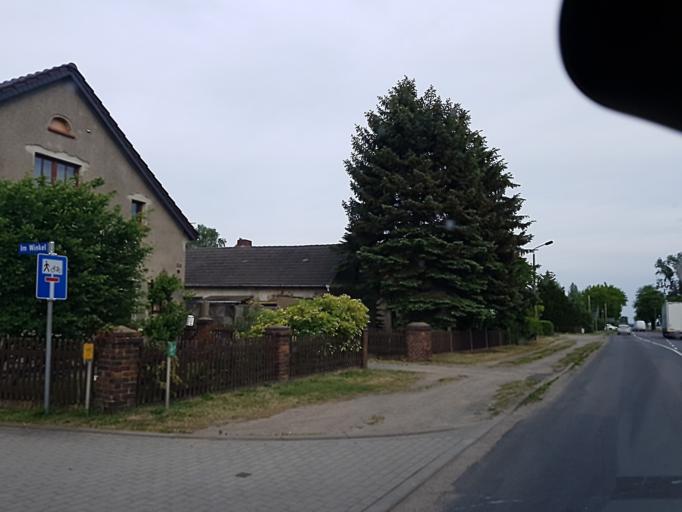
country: DE
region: Brandenburg
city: Herzberg
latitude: 51.6933
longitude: 13.2512
